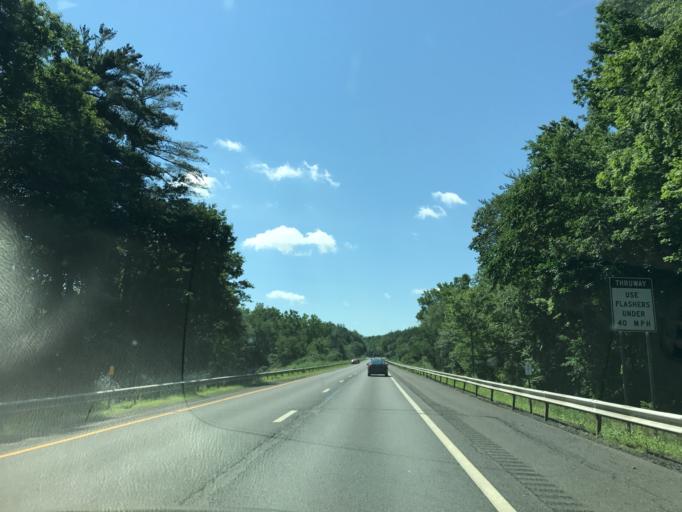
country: US
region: New York
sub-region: Rensselaer County
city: Nassau
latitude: 42.4548
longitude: -73.5782
